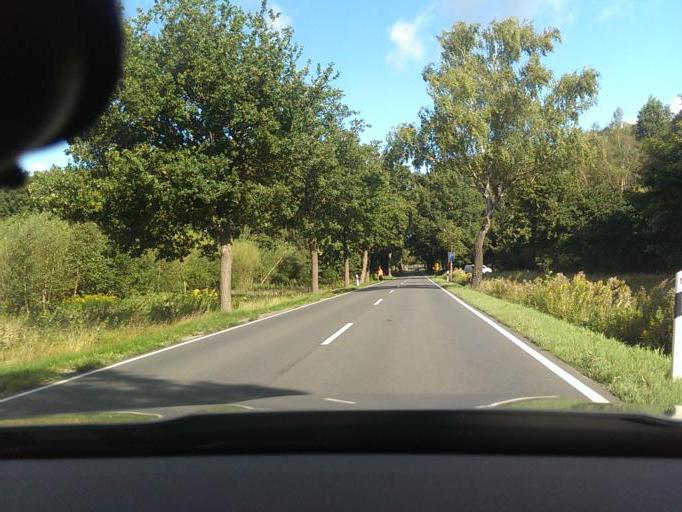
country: DE
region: Lower Saxony
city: Isernhagen Farster Bauerschaft
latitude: 52.4405
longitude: 9.8474
